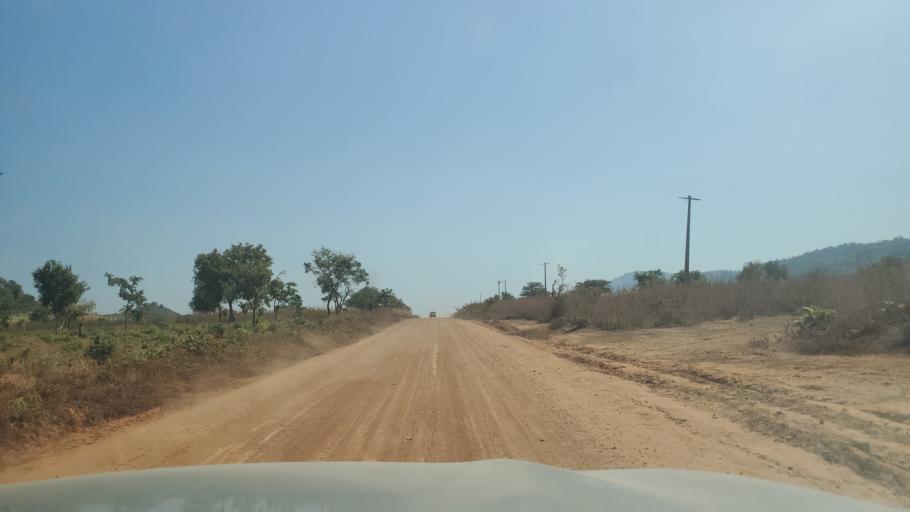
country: NG
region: Niger
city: Gawu Babangida
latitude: 9.2256
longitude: 6.8388
